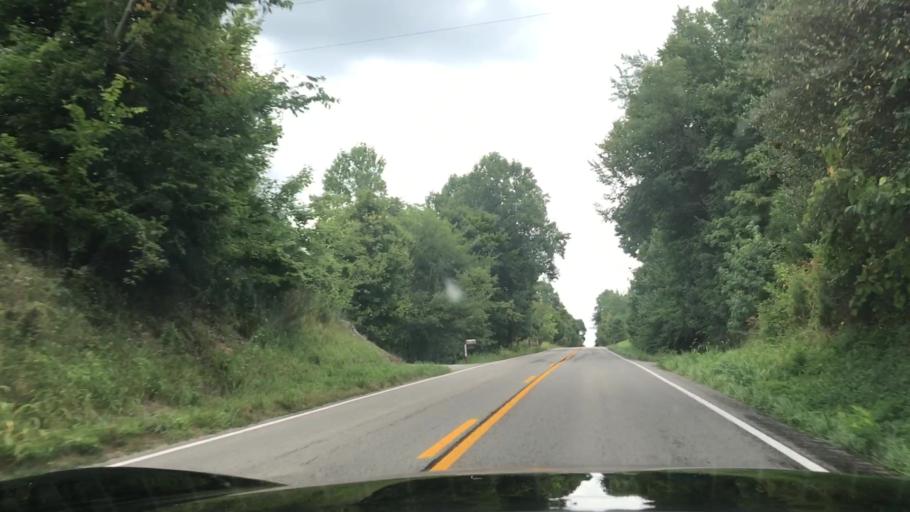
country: US
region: Kentucky
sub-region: Muhlenberg County
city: Central City
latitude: 37.2015
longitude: -86.9637
